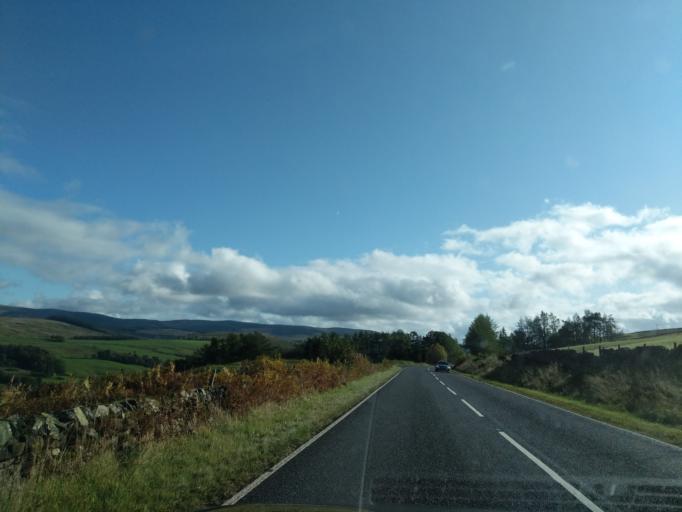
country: GB
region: Scotland
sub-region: Dumfries and Galloway
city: Moffat
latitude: 55.3582
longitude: -3.4729
